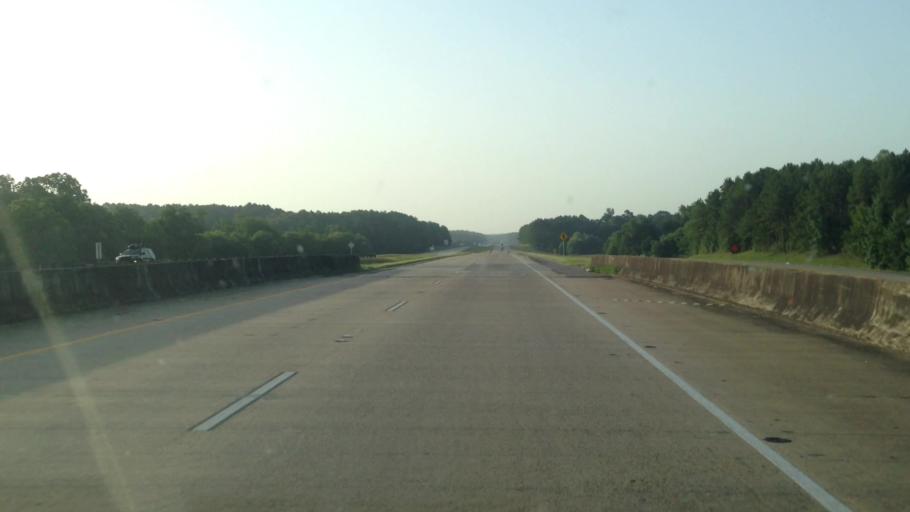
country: US
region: Louisiana
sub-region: Grant Parish
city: Colfax
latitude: 31.4944
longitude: -92.8617
